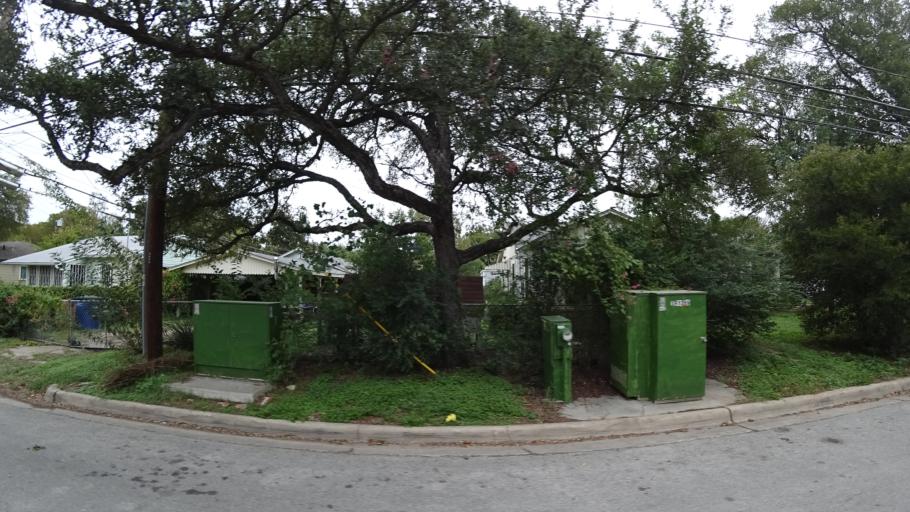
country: US
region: Texas
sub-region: Travis County
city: Austin
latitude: 30.2868
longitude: -97.7171
